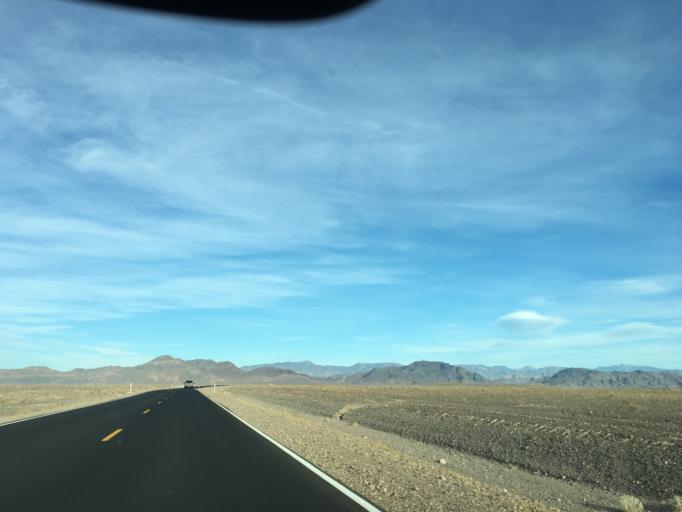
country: US
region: Nevada
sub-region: Nye County
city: Pahrump
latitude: 36.3493
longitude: -116.3217
